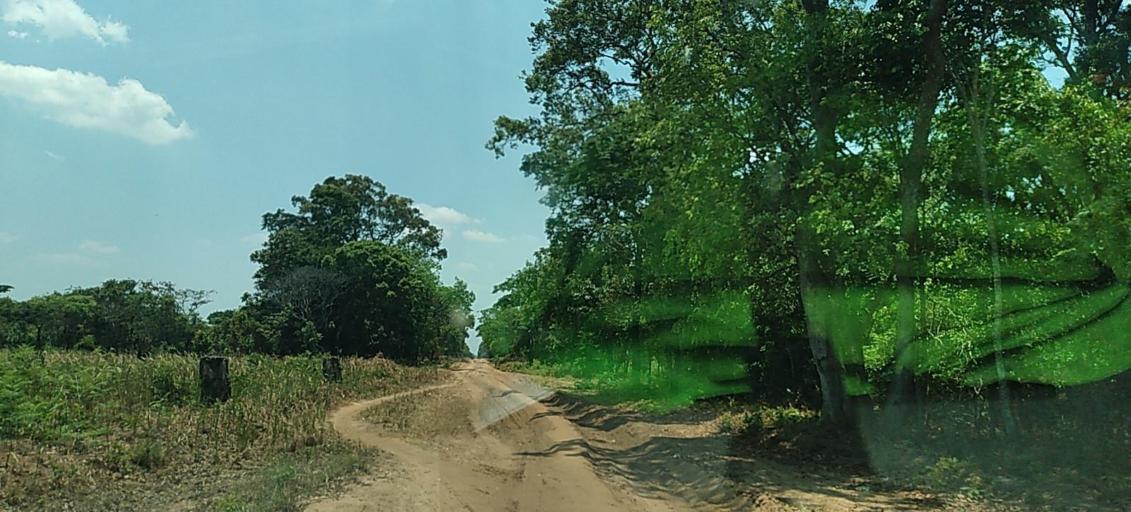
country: CD
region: Katanga
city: Kolwezi
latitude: -11.3890
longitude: 25.2212
